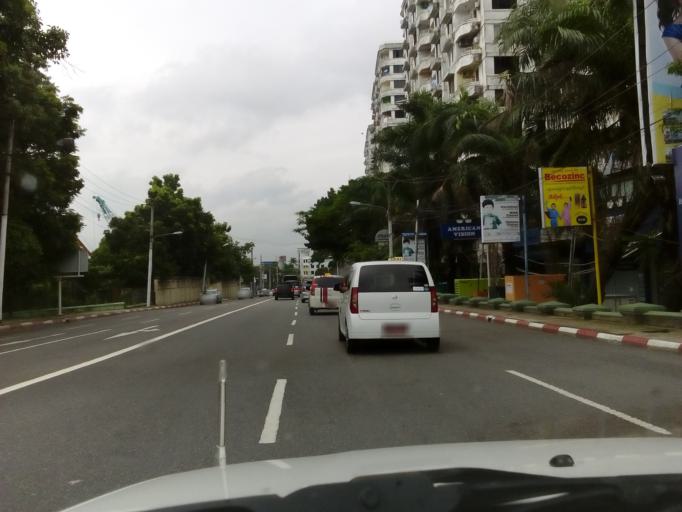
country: MM
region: Yangon
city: Yangon
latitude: 16.8155
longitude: 96.1560
